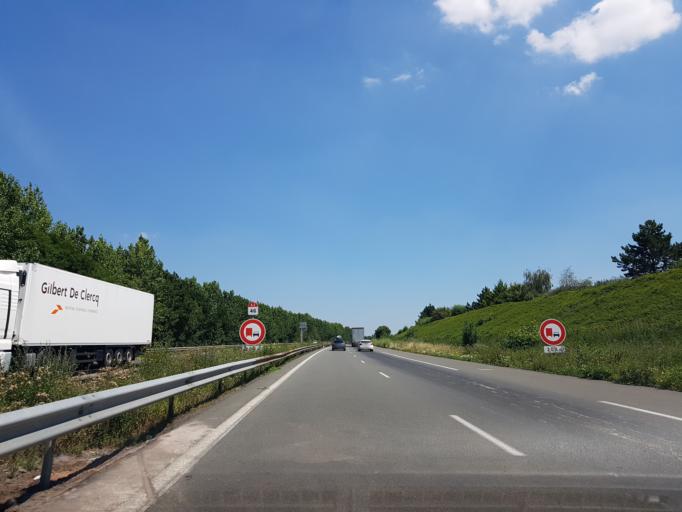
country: FR
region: Nord-Pas-de-Calais
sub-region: Departement du Nord
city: Lieu-Saint-Amand
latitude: 50.2774
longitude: 3.3398
